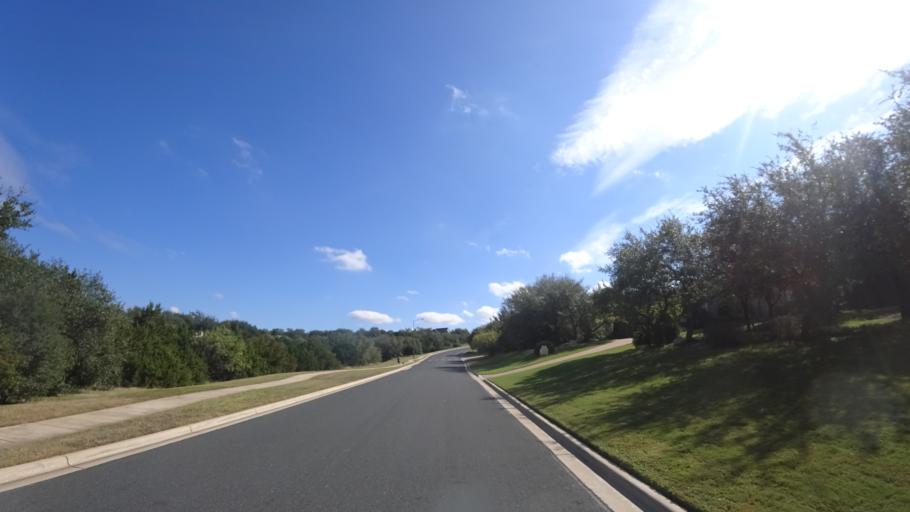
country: US
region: Texas
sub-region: Travis County
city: Hudson Bend
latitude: 30.3808
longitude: -97.9085
